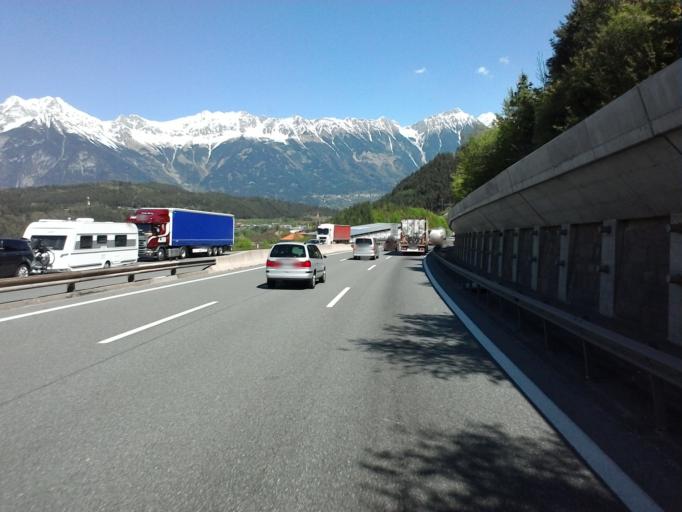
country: AT
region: Tyrol
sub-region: Politischer Bezirk Innsbruck Land
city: Mutters
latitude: 47.2244
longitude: 11.3921
